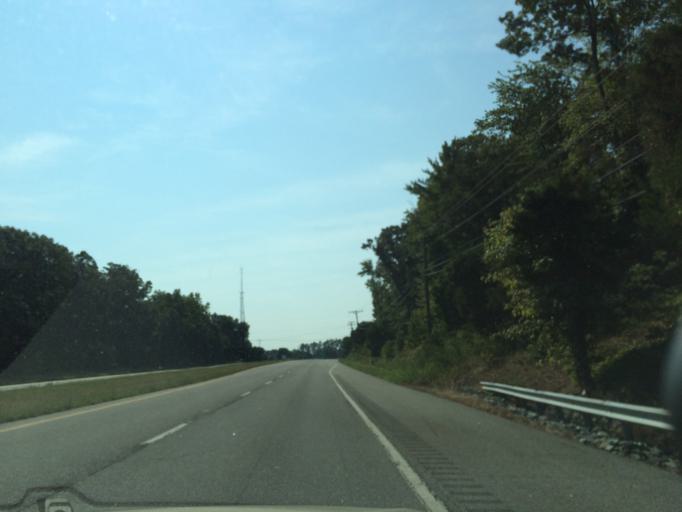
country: US
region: Maryland
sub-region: Charles County
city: La Plata
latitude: 38.4164
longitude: -76.9590
